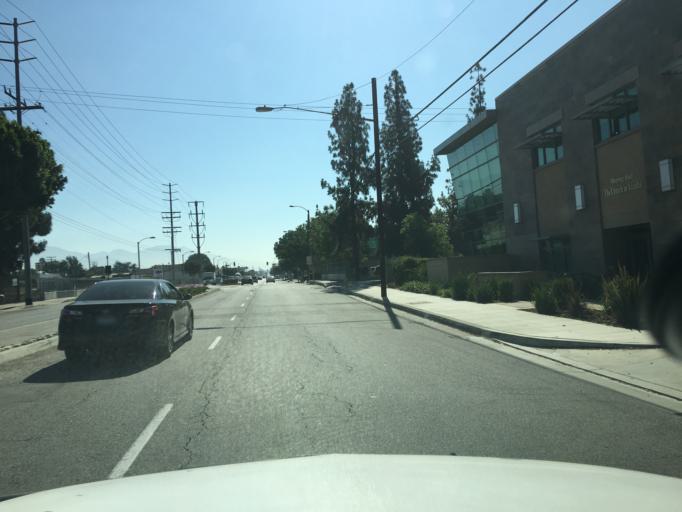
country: US
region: California
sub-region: Los Angeles County
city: North El Monte
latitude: 34.1092
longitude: -118.0176
